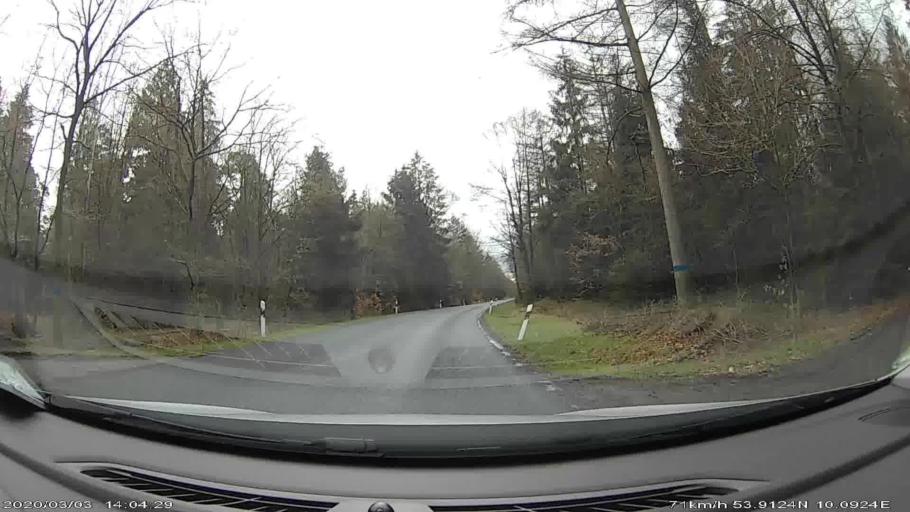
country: DE
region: Schleswig-Holstein
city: Hartenholm
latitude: 53.9118
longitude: 10.0922
